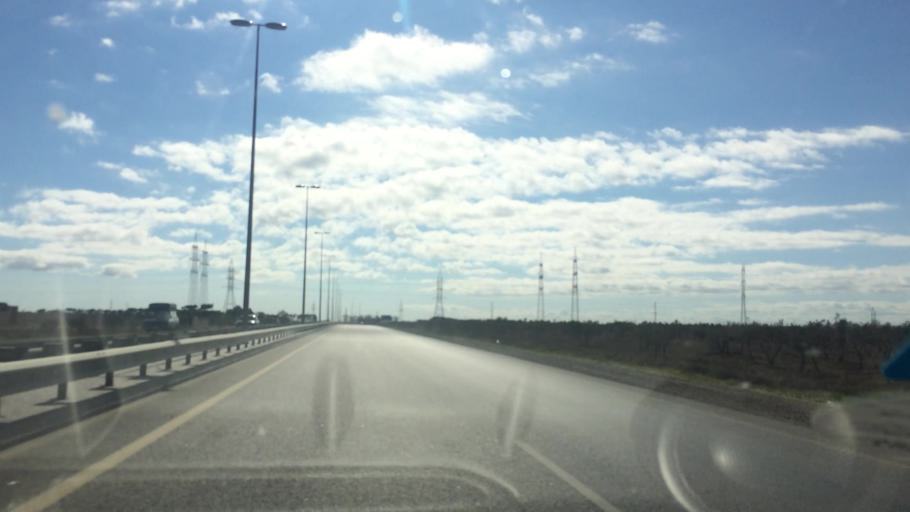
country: AZ
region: Baki
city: Qala
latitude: 40.4399
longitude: 50.1818
